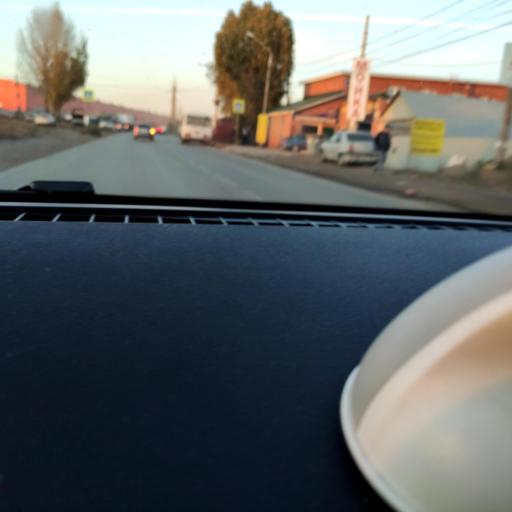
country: RU
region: Samara
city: Petra-Dubrava
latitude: 53.2520
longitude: 50.3103
